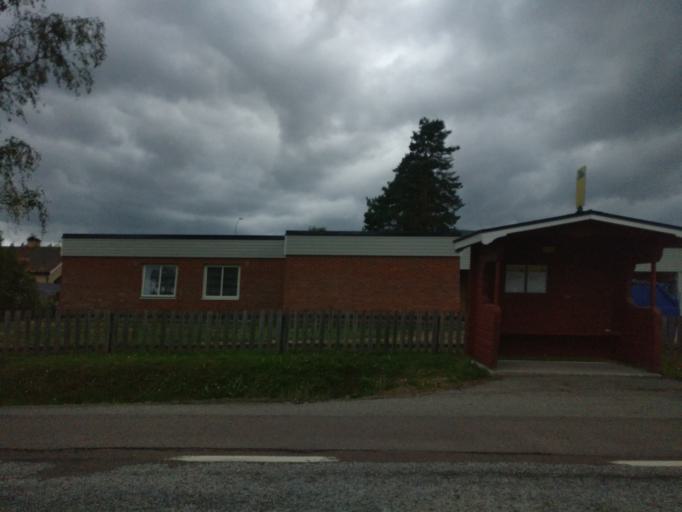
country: SE
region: Vaermland
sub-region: Torsby Kommun
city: Torsby
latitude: 60.6122
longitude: 13.0466
